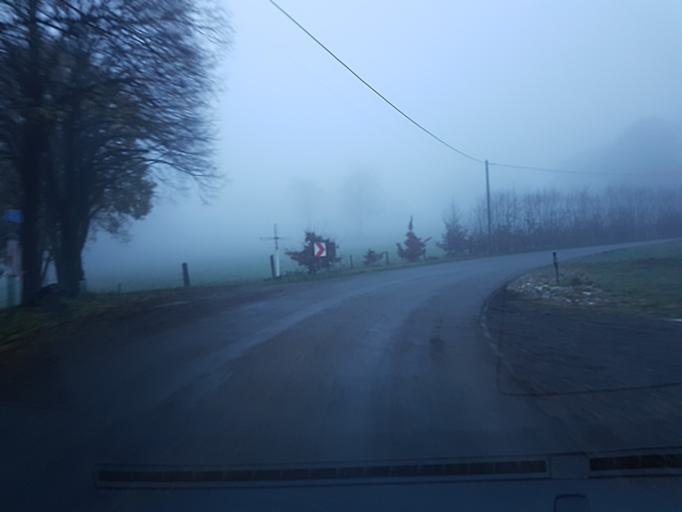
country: BE
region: Wallonia
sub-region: Province de Liege
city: Theux
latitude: 50.5081
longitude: 5.8028
